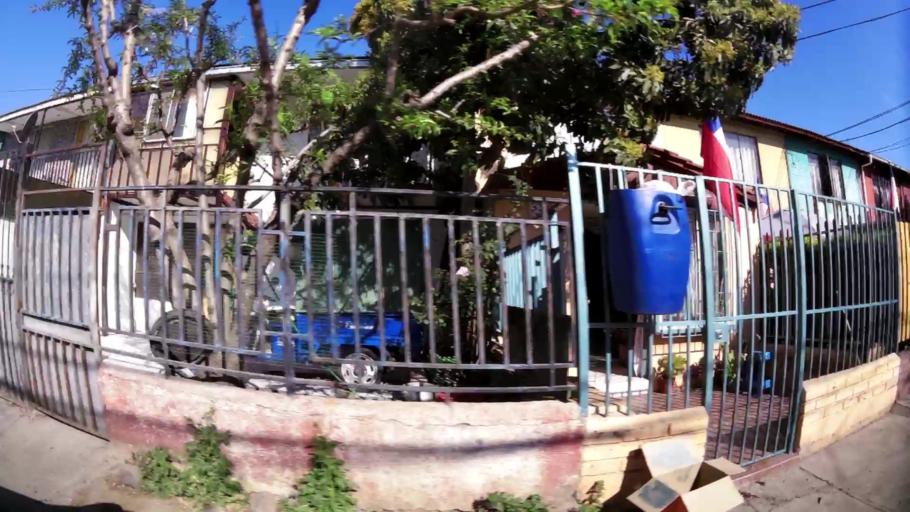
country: CL
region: Santiago Metropolitan
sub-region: Provincia de Santiago
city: Lo Prado
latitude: -33.4894
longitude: -70.7699
